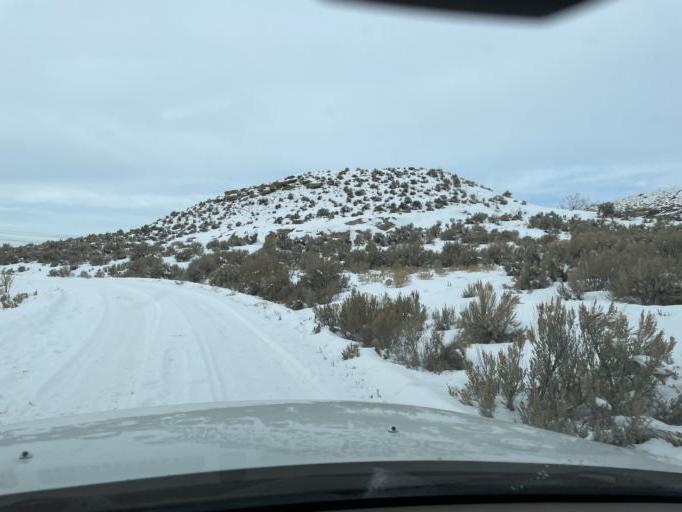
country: US
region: Colorado
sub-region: Moffat County
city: Craig
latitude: 40.4752
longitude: -107.5833
